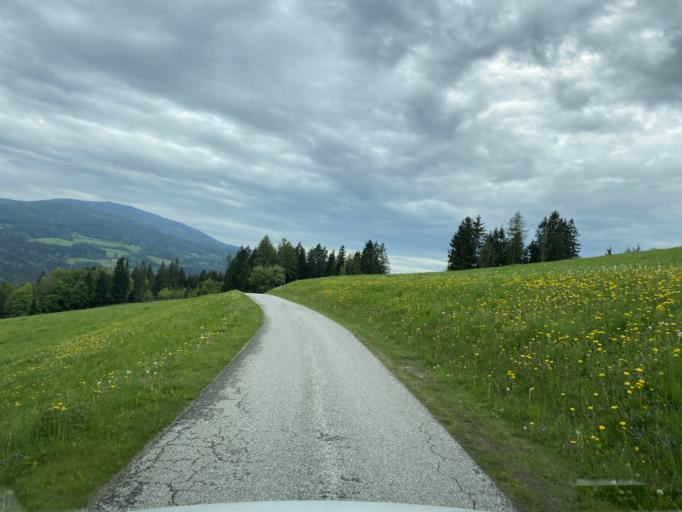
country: AT
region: Styria
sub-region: Politischer Bezirk Weiz
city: Koglhof
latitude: 47.3331
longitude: 15.6766
